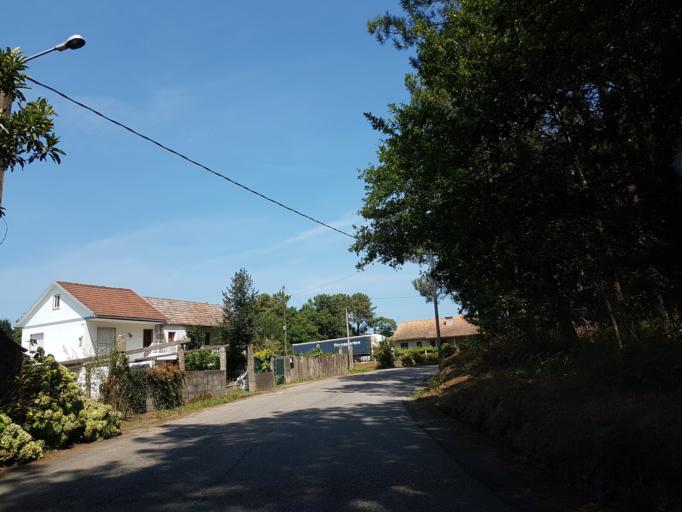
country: ES
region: Galicia
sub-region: Provincia de Pontevedra
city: Porrino
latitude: 42.2085
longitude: -8.6203
